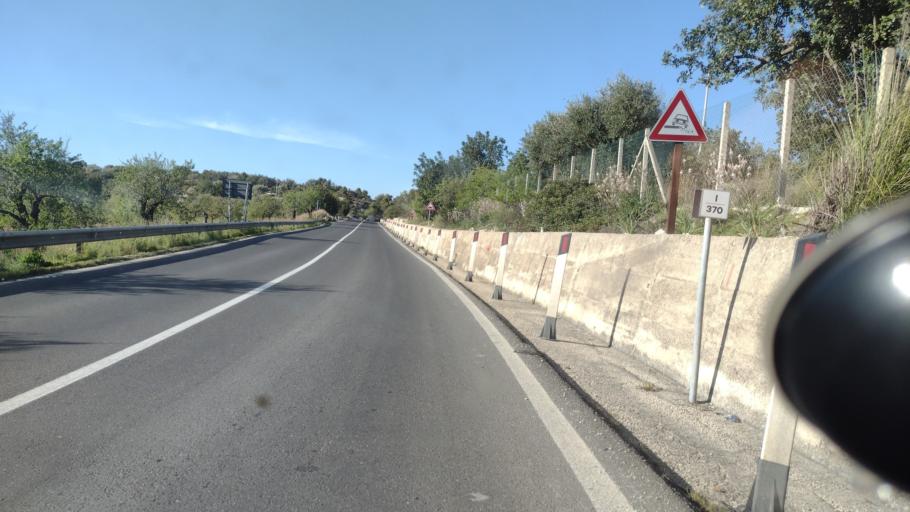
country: IT
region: Sicily
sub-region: Provincia di Siracusa
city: Noto
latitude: 36.8635
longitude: 15.0245
